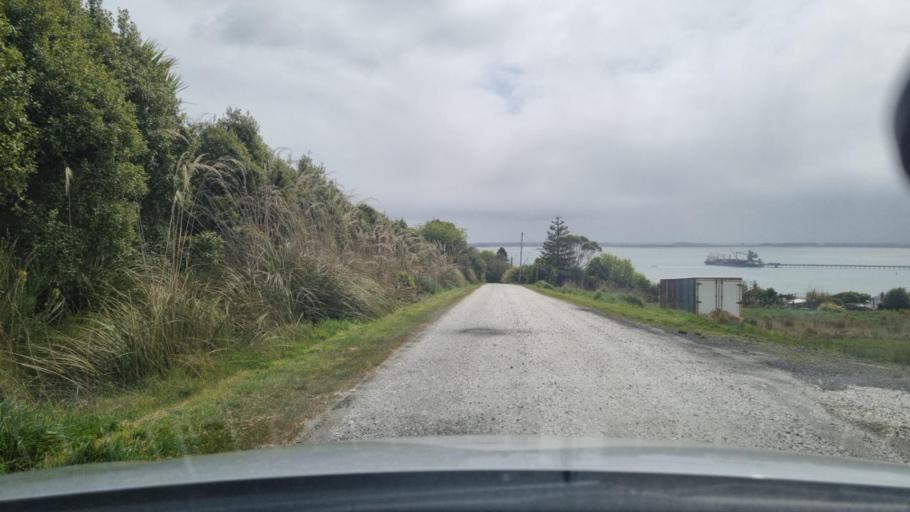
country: NZ
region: Southland
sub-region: Invercargill City
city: Bluff
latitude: -46.6082
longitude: 168.3514
